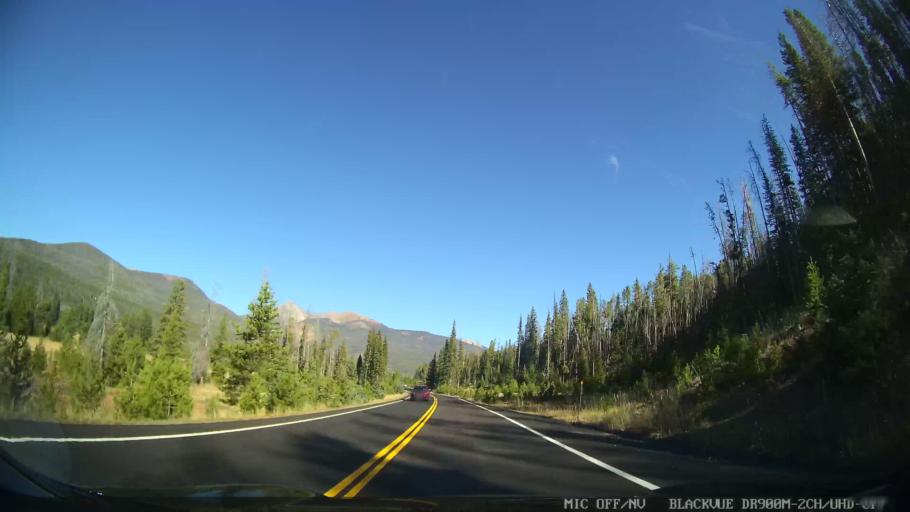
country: US
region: Colorado
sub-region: Grand County
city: Granby
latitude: 40.3335
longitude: -105.8550
